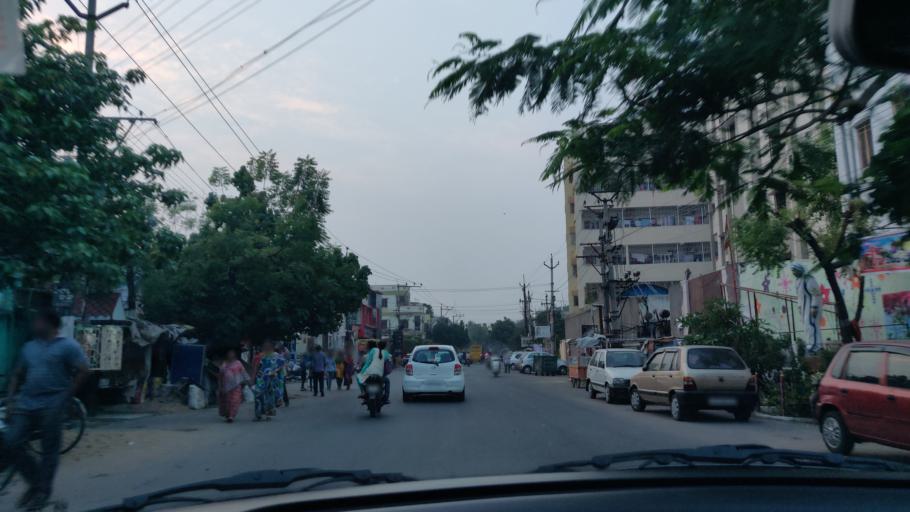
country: IN
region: Andhra Pradesh
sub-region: Krishna
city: Vijayawada
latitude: 16.5069
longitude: 80.6389
